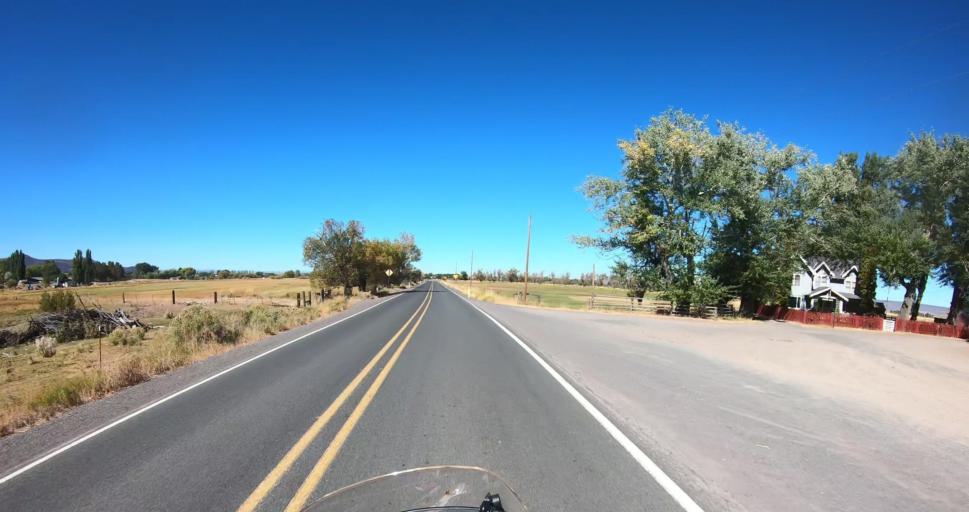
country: US
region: Oregon
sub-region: Lake County
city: Lakeview
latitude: 42.6851
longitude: -120.5286
